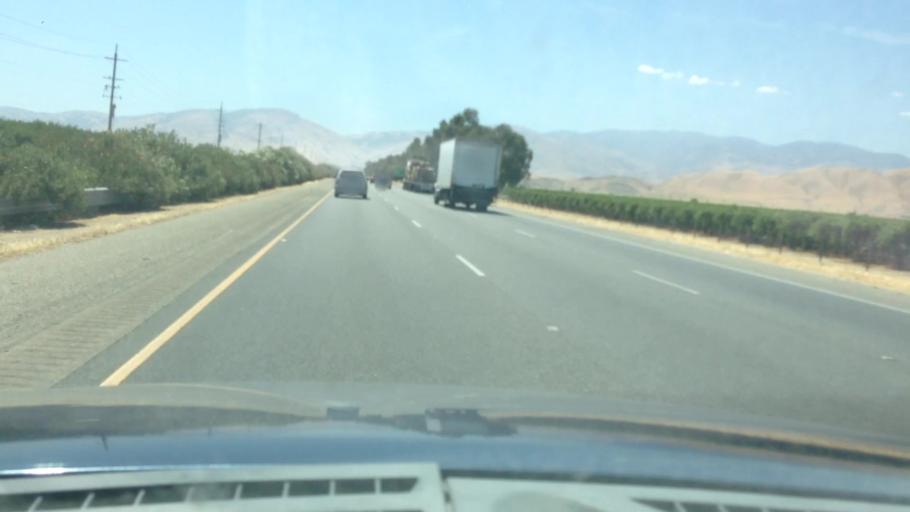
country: US
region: California
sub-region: Kern County
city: Weedpatch
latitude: 35.0501
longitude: -118.9654
